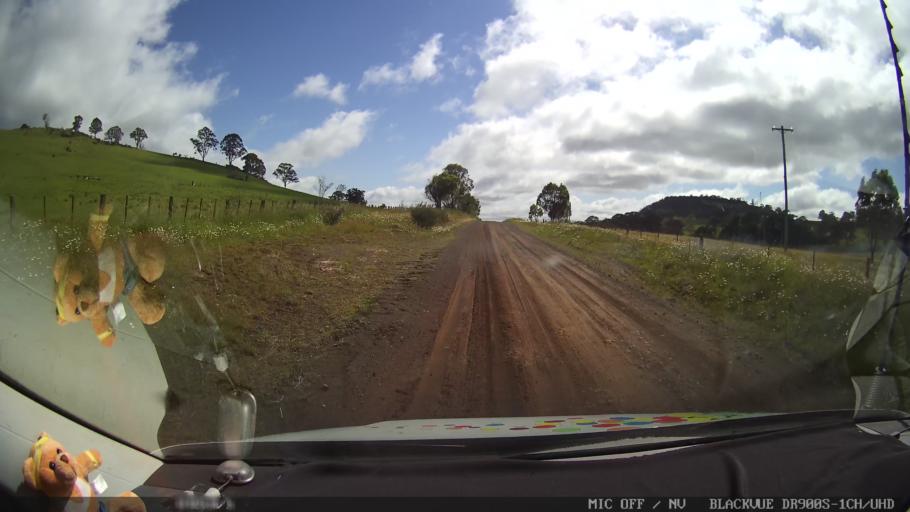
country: AU
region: New South Wales
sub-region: Guyra
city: Guyra
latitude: -30.0078
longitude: 151.6645
